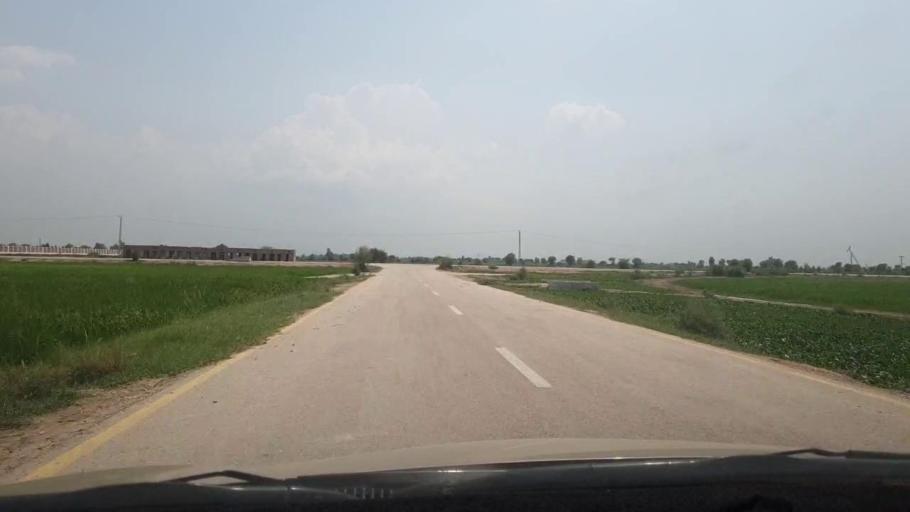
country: PK
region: Sindh
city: Naudero
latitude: 27.6958
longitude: 68.3336
